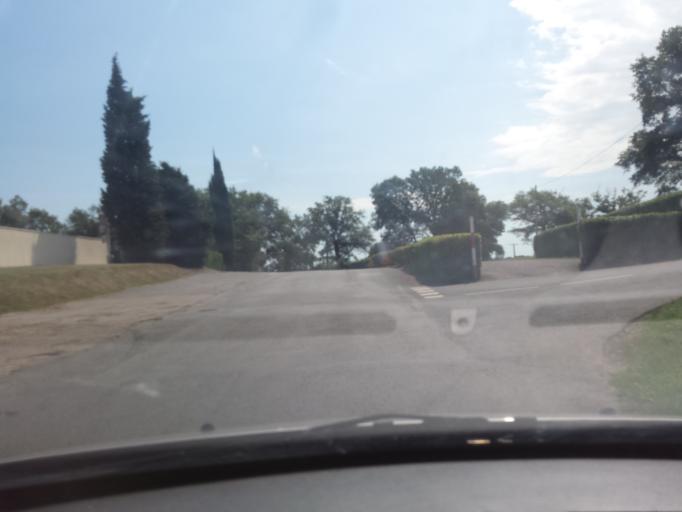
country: FR
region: Poitou-Charentes
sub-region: Departement de la Vienne
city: Availles-Limouzine
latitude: 46.1016
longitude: 0.7086
